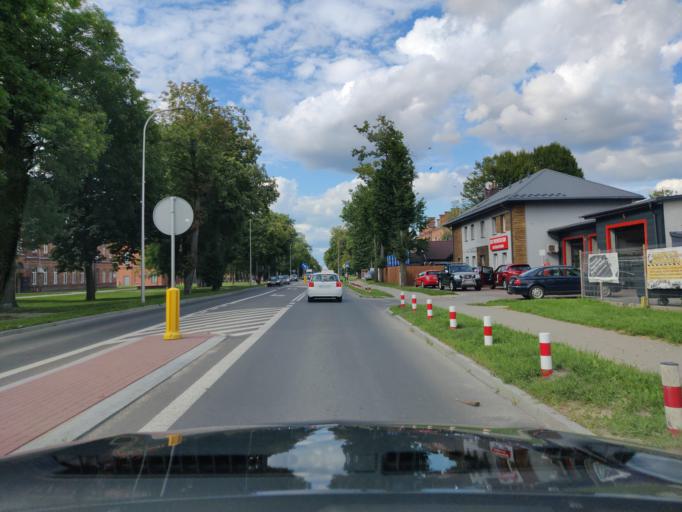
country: PL
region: Podlasie
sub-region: Powiat zambrowski
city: Zambrow
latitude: 52.9666
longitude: 22.2442
